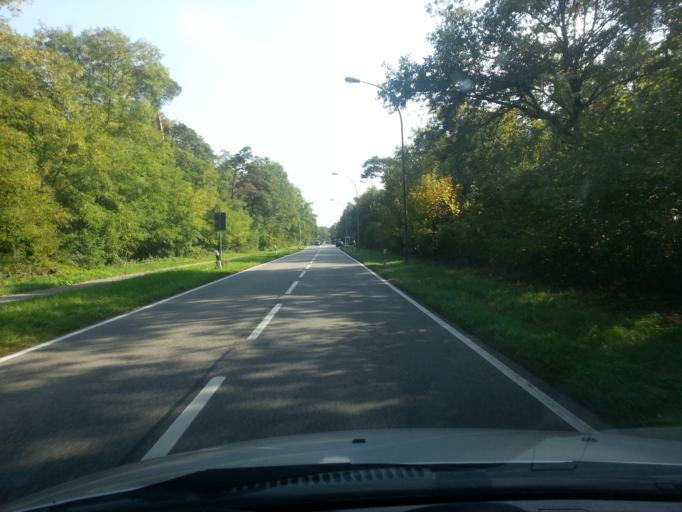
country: DE
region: Rheinland-Pfalz
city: Schifferstadt
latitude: 49.3676
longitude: 8.3905
